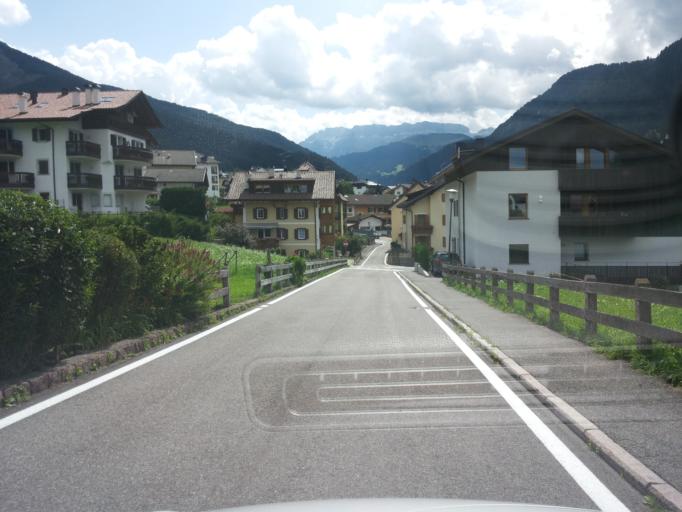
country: IT
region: Trentino-Alto Adige
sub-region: Bolzano
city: Ortisei
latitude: 46.5757
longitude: 11.6652
